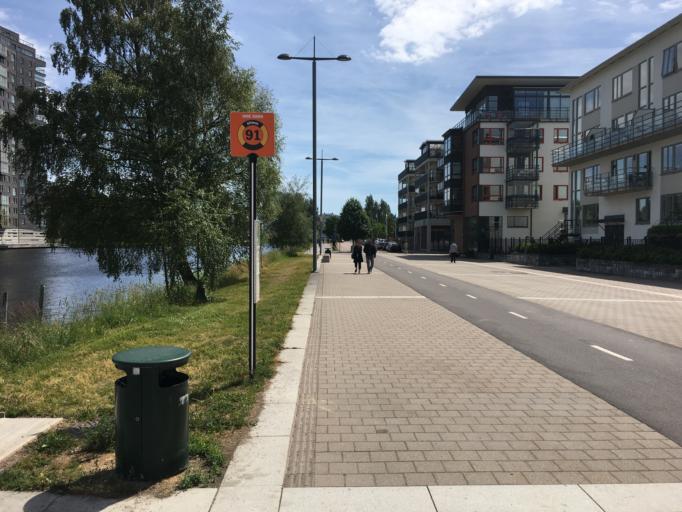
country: SE
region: Vaermland
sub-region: Karlstads Kommun
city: Karlstad
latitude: 59.3755
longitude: 13.5074
